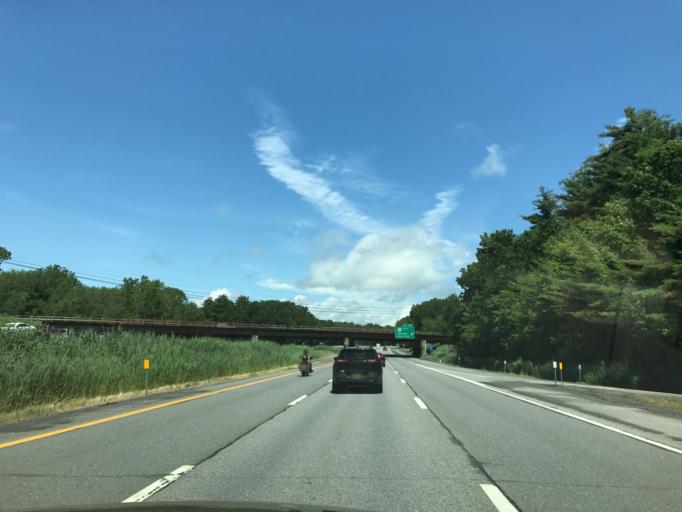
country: US
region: New York
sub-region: Warren County
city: West Glens Falls
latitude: 43.2339
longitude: -73.6921
